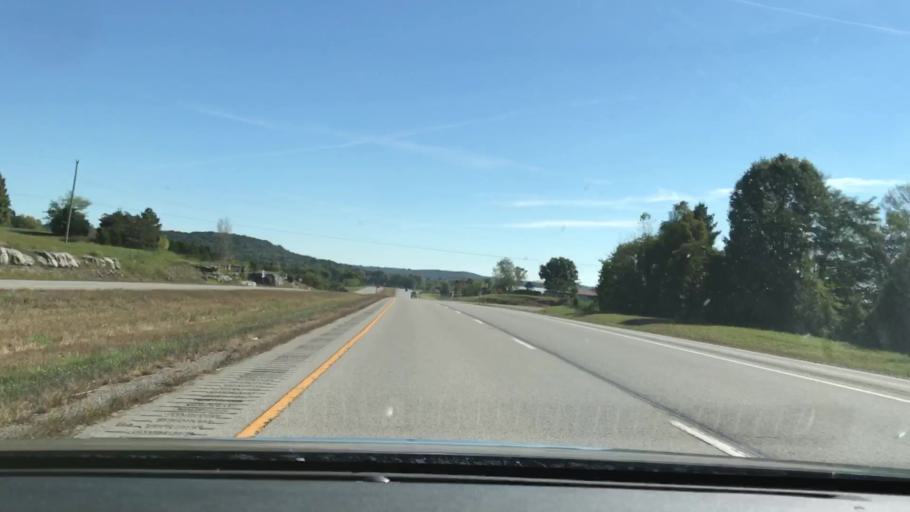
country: US
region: Kentucky
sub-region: Todd County
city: Elkton
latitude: 36.8458
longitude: -87.2901
